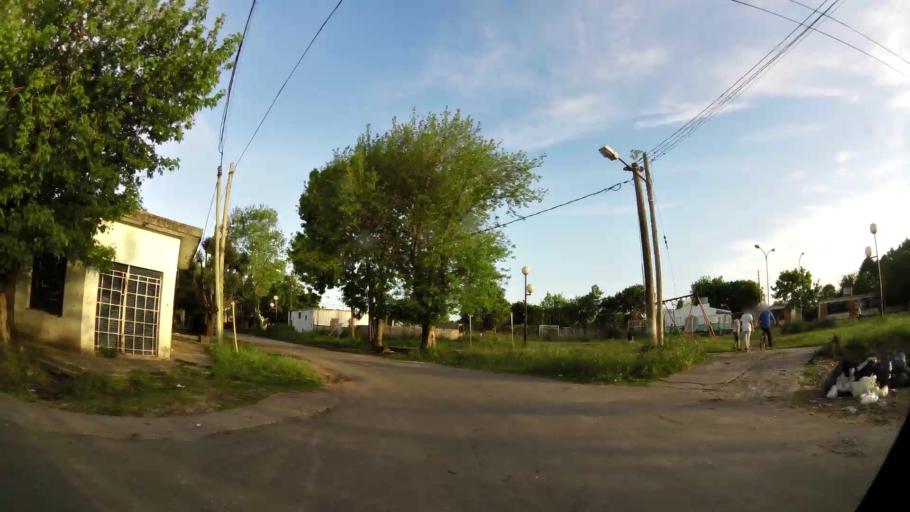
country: AR
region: Buenos Aires
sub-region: Partido de Quilmes
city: Quilmes
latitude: -34.7764
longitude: -58.2016
